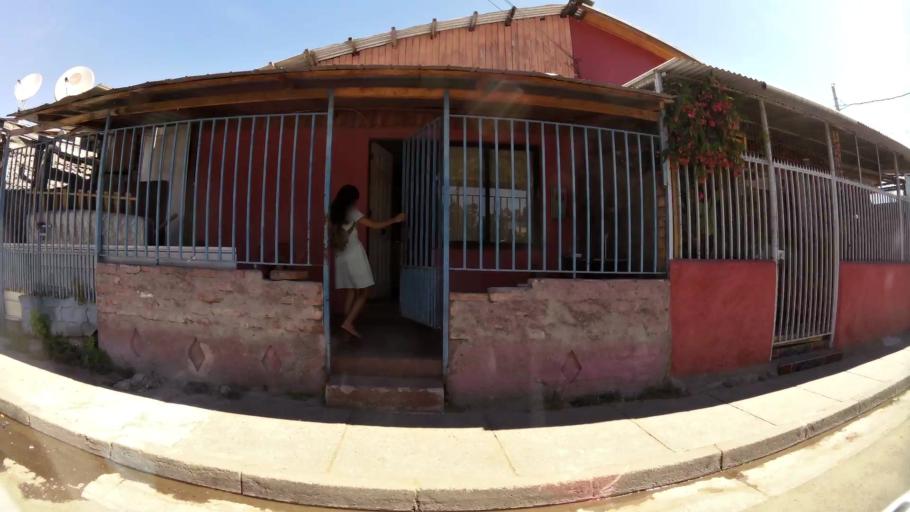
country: CL
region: O'Higgins
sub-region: Provincia de Colchagua
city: Chimbarongo
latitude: -34.5742
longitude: -70.9847
